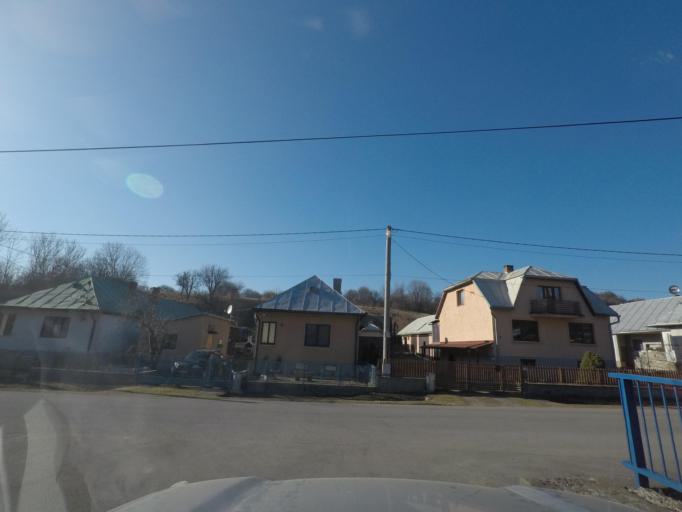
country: SK
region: Presovsky
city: Medzilaborce
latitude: 49.1650
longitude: 22.0373
